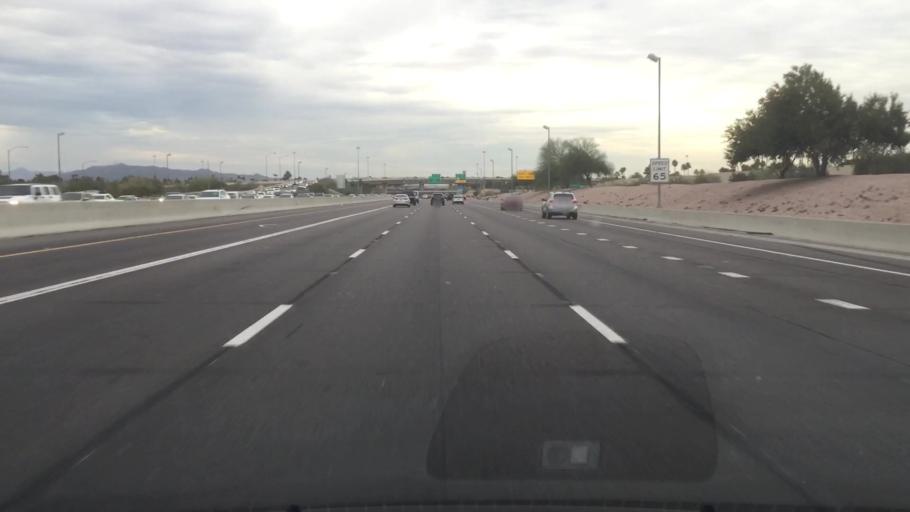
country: US
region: Arizona
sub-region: Maricopa County
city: Tempe
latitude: 33.3868
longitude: -111.8832
